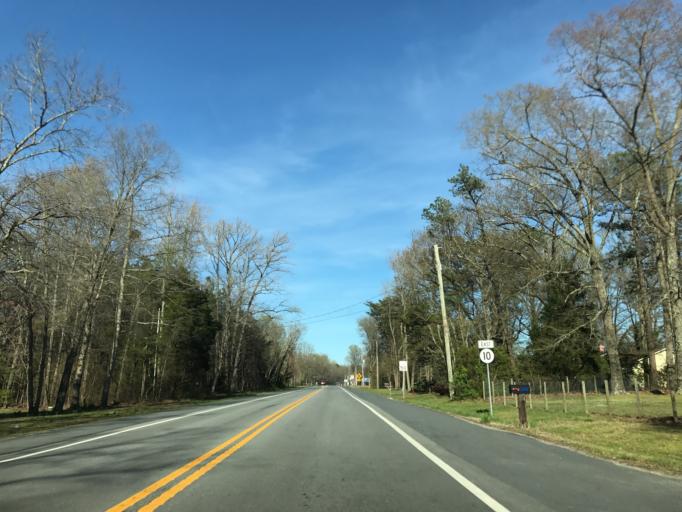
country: US
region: Maryland
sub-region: Caroline County
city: Greensboro
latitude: 39.0297
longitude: -75.7385
